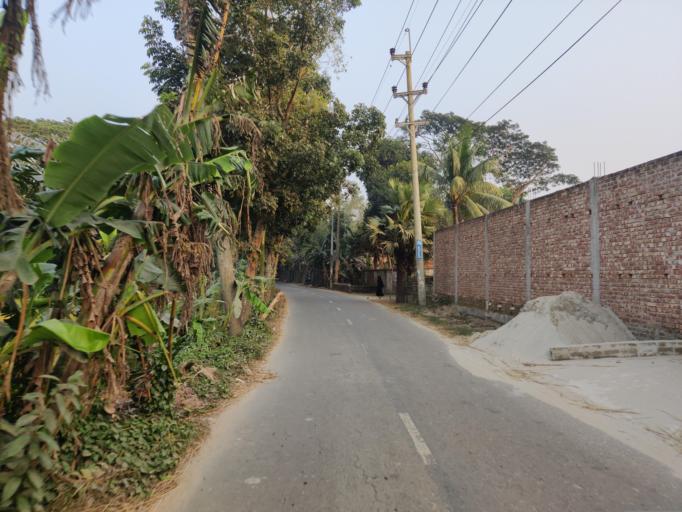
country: BD
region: Dhaka
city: Bajitpur
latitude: 24.1583
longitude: 90.7596
